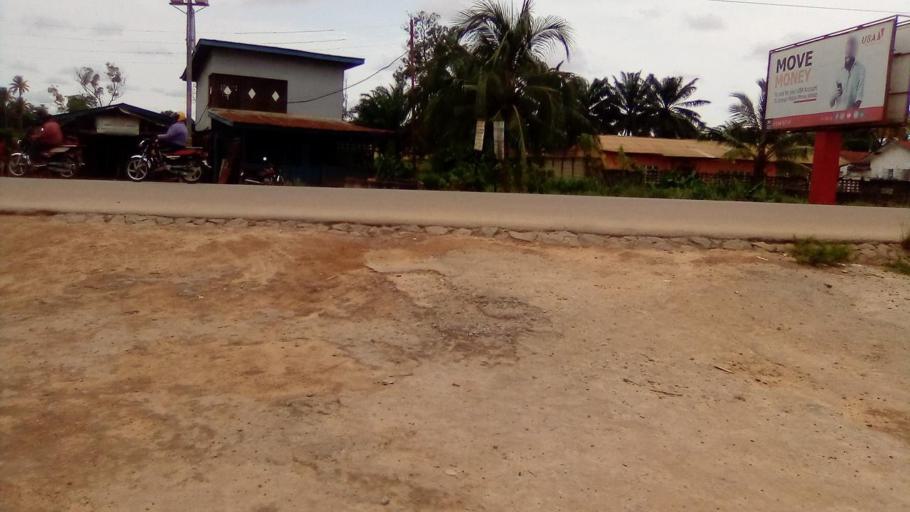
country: SL
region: Southern Province
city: Bo
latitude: 7.9514
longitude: -11.7503
